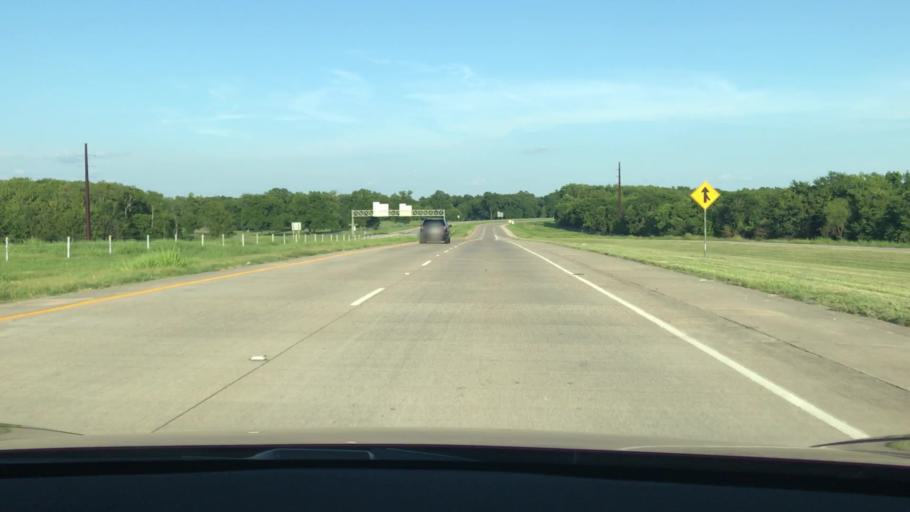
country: US
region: Louisiana
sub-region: Bossier Parish
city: Bossier City
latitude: 32.4108
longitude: -93.7232
